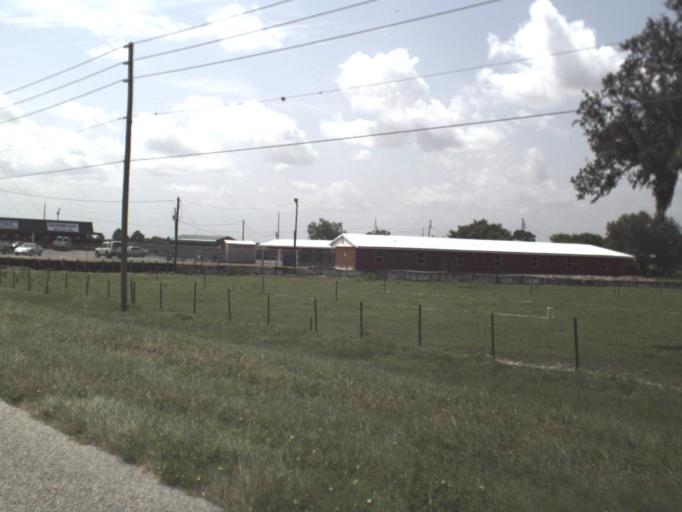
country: US
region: Florida
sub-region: Polk County
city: Lake Wales
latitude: 27.8819
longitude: -81.5986
